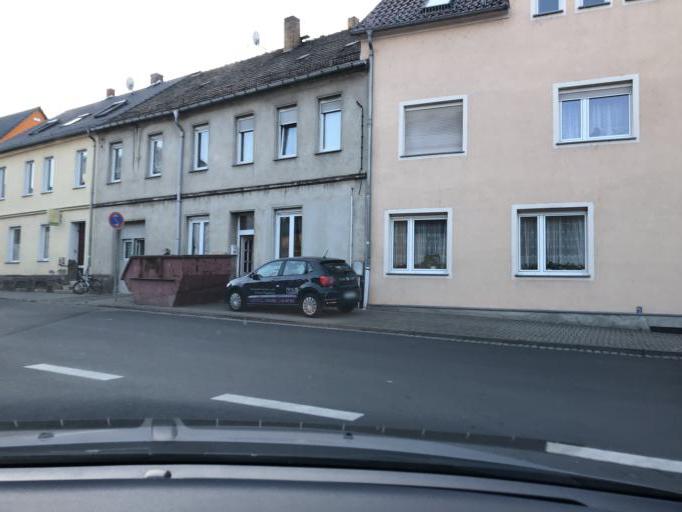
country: DE
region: Saxony
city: Nerchau
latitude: 51.2716
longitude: 12.7894
